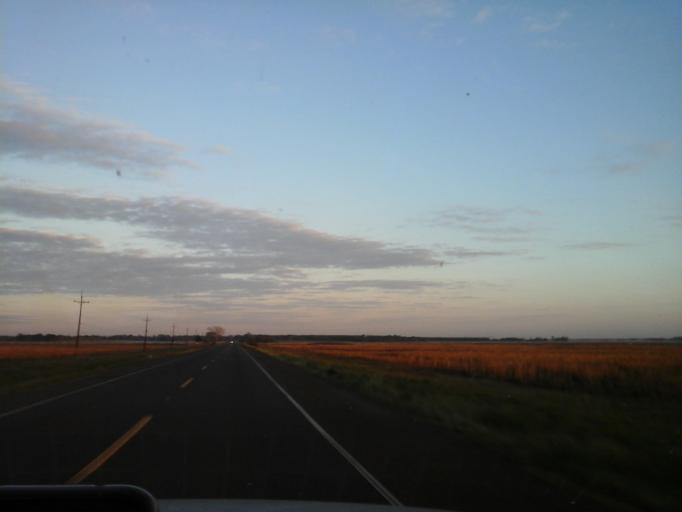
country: PY
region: Itapua
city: General Delgado
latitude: -27.0826
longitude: -56.5589
